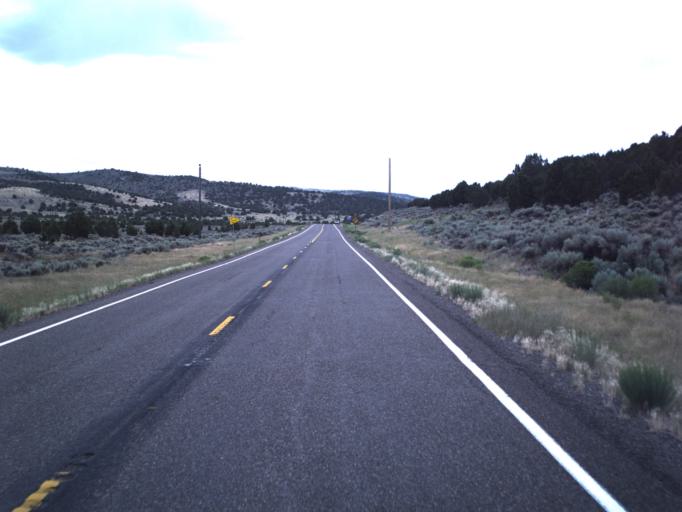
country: US
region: Utah
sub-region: Wayne County
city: Loa
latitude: 38.5522
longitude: -111.8360
